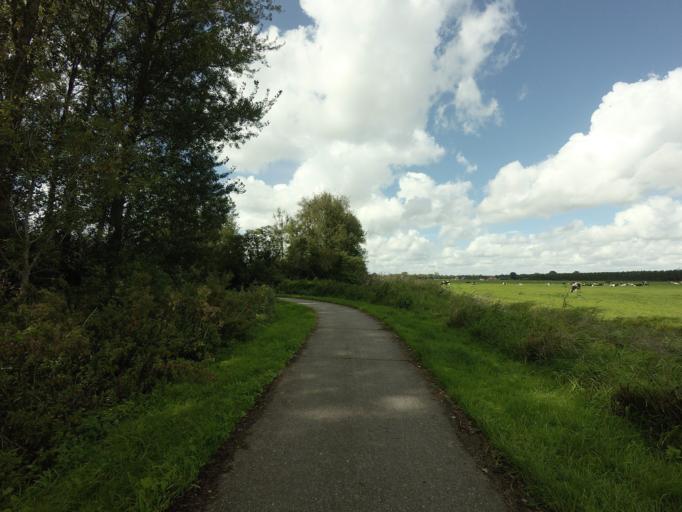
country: NL
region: North Holland
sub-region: Gemeente Purmerend
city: Purmerend
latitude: 52.4776
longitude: 4.9783
